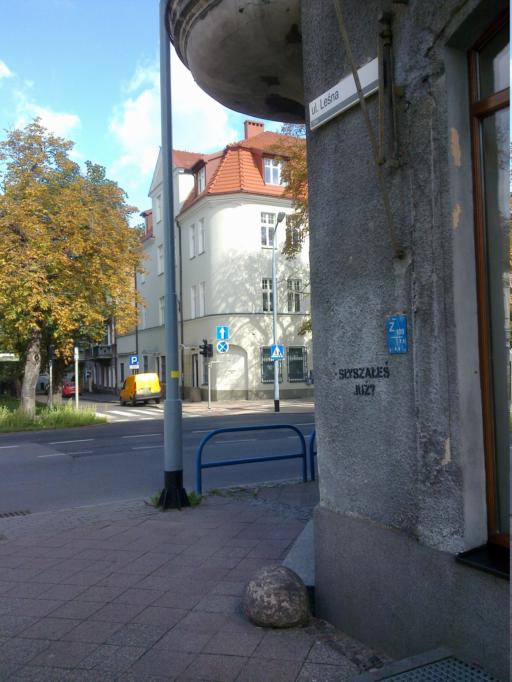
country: PL
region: Pomeranian Voivodeship
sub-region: Sopot
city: Sopot
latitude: 54.4087
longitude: 18.5568
